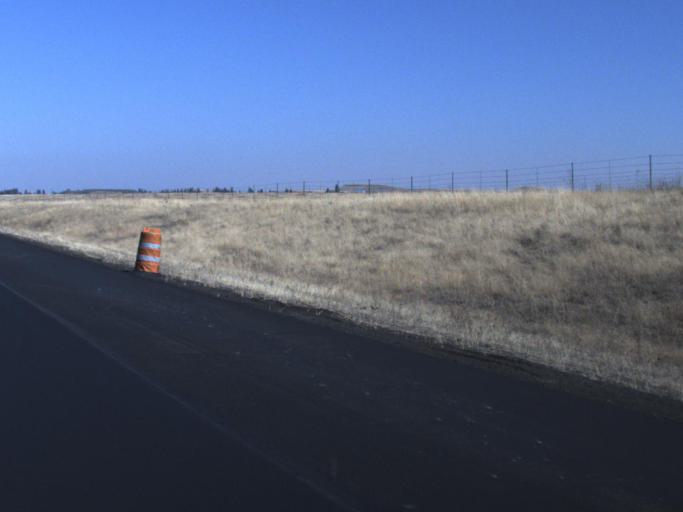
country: US
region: Washington
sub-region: Spokane County
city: Medical Lake
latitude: 47.3309
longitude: -117.9232
